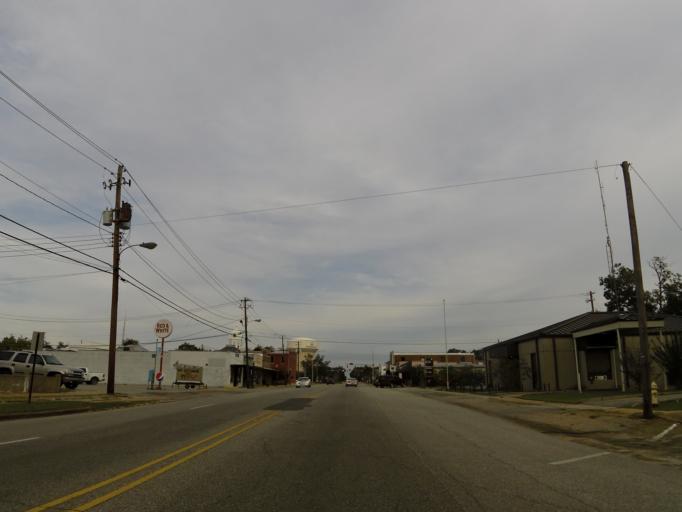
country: US
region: Alabama
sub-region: Monroe County
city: Monroeville
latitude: 31.5266
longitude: -87.3268
